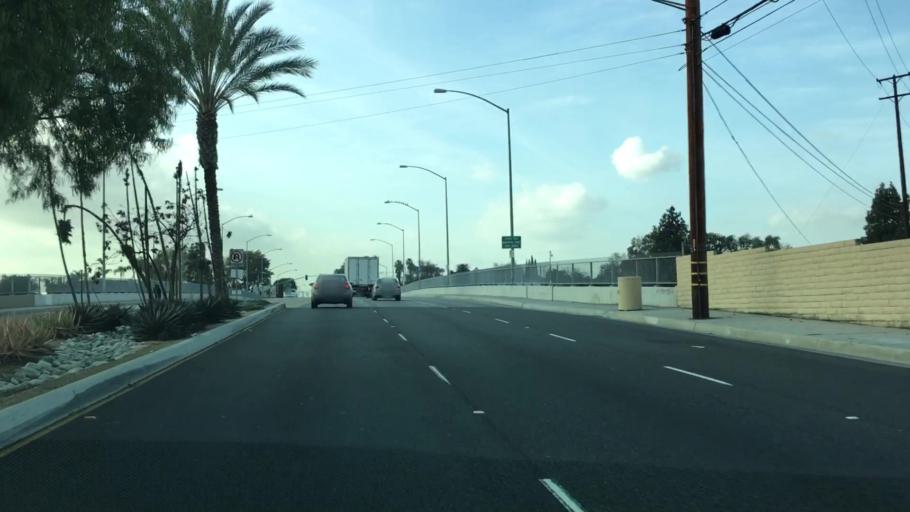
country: US
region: California
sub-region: Los Angeles County
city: Montebello
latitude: 34.0137
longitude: -118.0907
